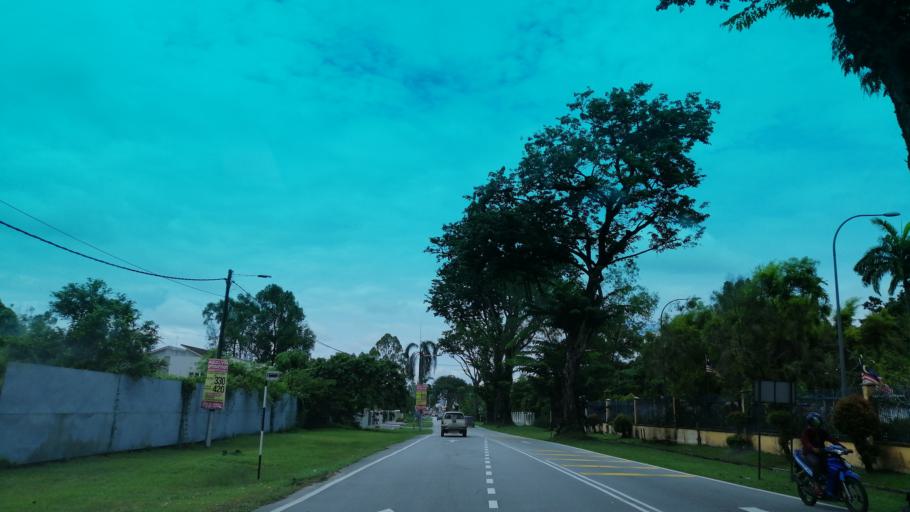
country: MY
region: Perak
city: Taiping
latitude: 4.8616
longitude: 100.7357
